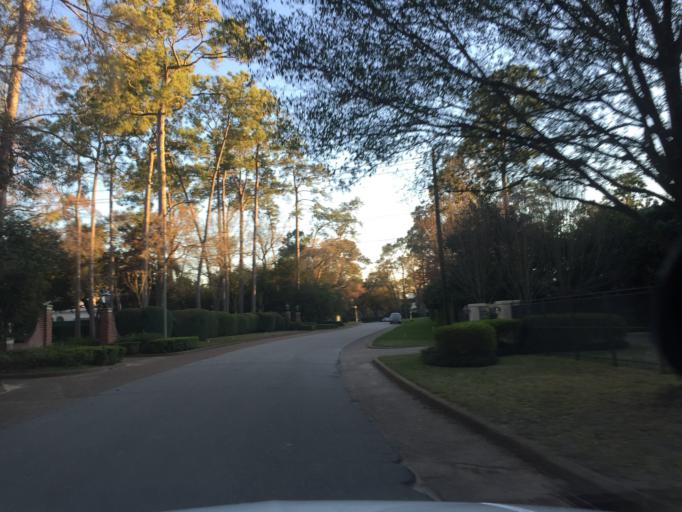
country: US
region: Texas
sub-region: Harris County
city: West University Place
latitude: 29.7554
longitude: -95.4351
